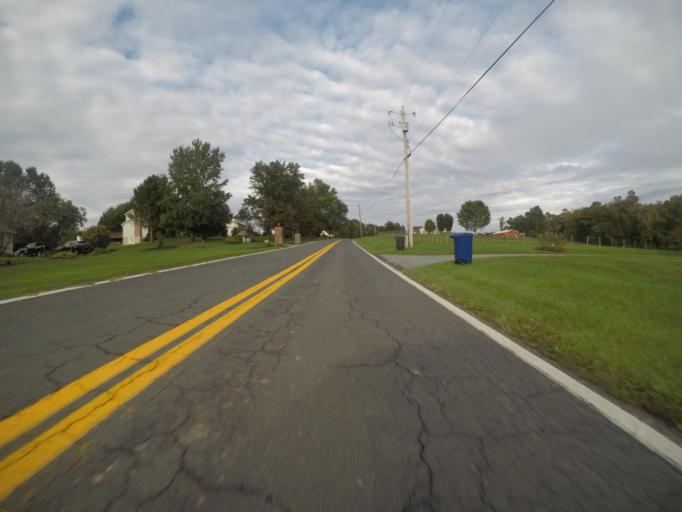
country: US
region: Maryland
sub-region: Carroll County
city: Hampstead
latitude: 39.5593
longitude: -76.8636
